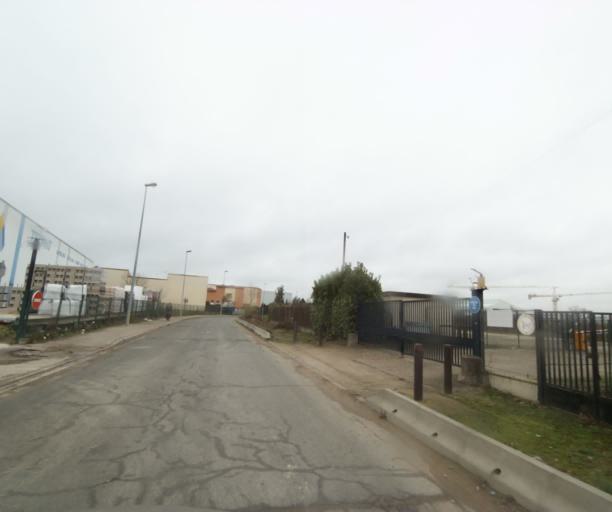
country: FR
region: Ile-de-France
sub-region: Departement du Val-de-Marne
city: Ablon-sur-Seine
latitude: 48.7310
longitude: 2.4365
